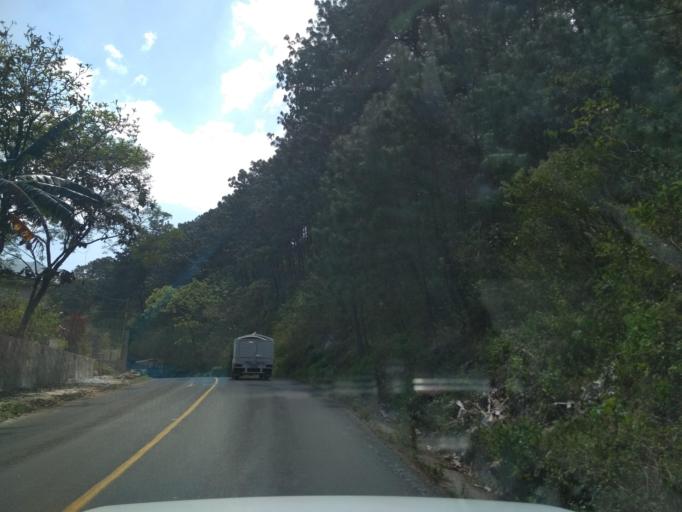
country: MX
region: Veracruz
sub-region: Tlilapan
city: Tonalixco
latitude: 18.7797
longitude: -97.0839
